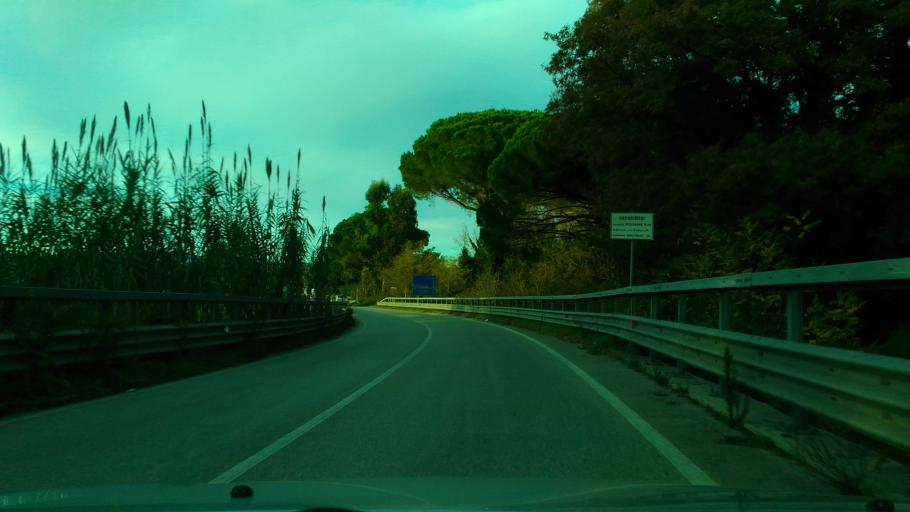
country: IT
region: Tuscany
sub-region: Provincia di Livorno
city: S.P. in Palazzi
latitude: 43.3714
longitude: 10.5055
